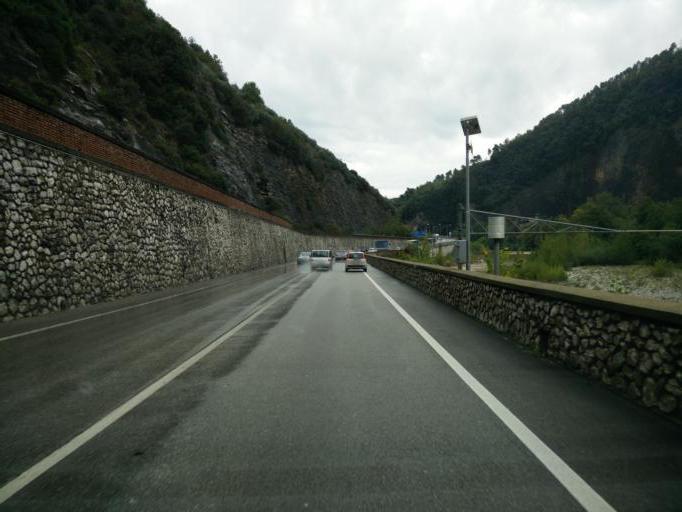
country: IT
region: Tuscany
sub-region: Provincia di Lucca
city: Valdottavo
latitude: 43.9294
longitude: 10.5143
